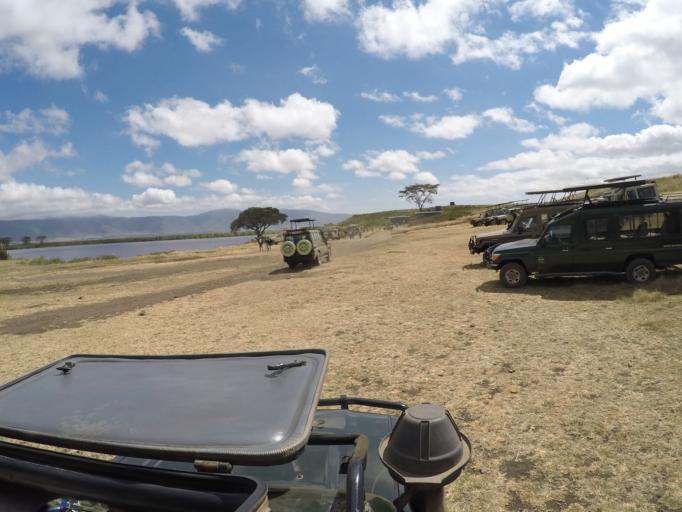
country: TZ
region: Arusha
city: Ngorongoro
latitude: -3.2107
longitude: 35.6021
